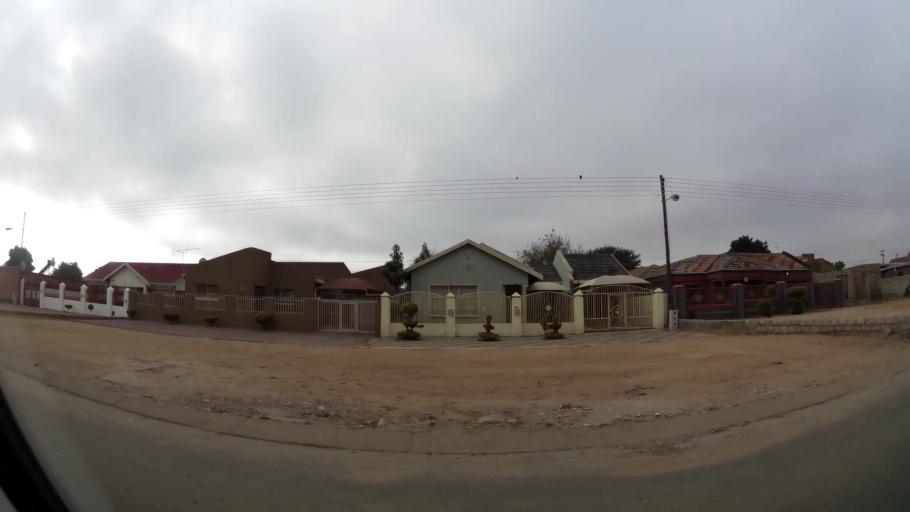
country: ZA
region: Limpopo
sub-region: Capricorn District Municipality
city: Polokwane
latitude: -23.8338
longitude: 29.3827
